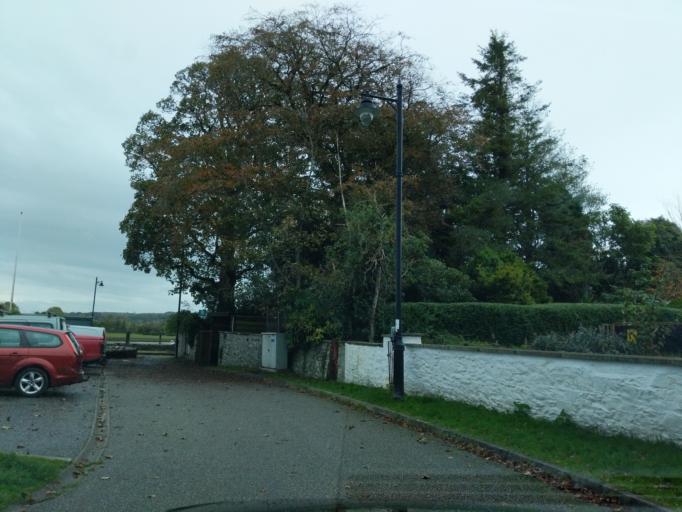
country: GB
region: Scotland
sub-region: Dumfries and Galloway
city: Kirkcudbright
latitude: 54.8370
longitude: -4.0567
